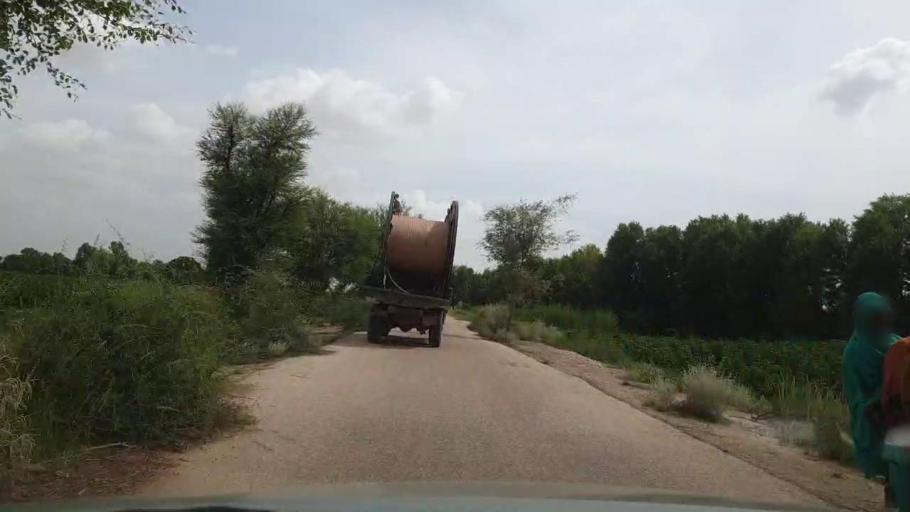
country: PK
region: Sindh
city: Kot Diji
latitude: 27.1567
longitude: 69.0352
